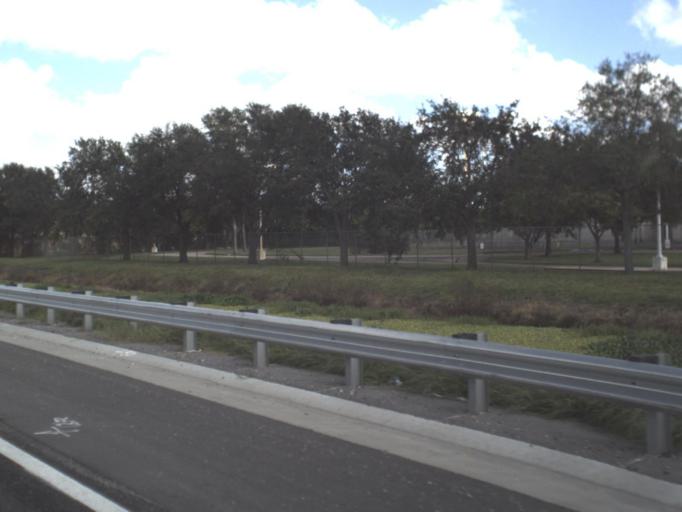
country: US
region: Florida
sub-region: Broward County
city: Miramar
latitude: 25.9794
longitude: -80.2298
